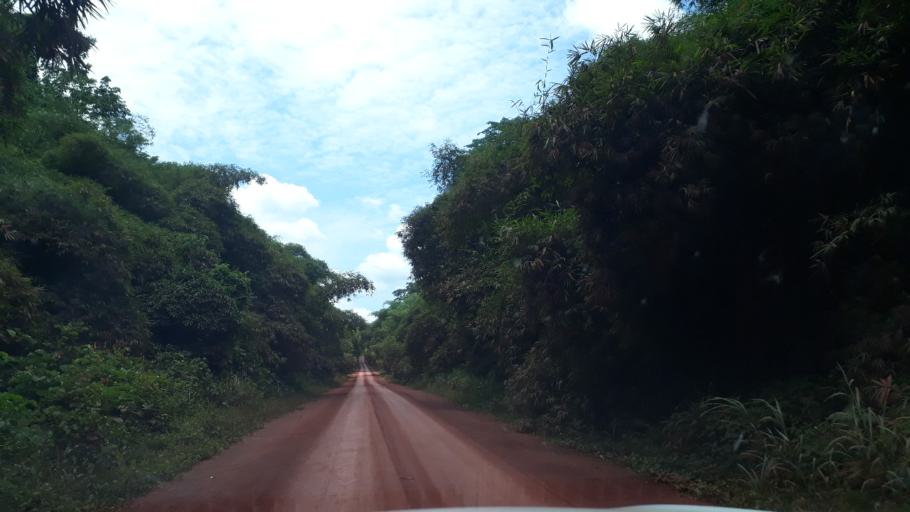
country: CD
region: Eastern Province
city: Kisangani
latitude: 0.5471
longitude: 25.8323
